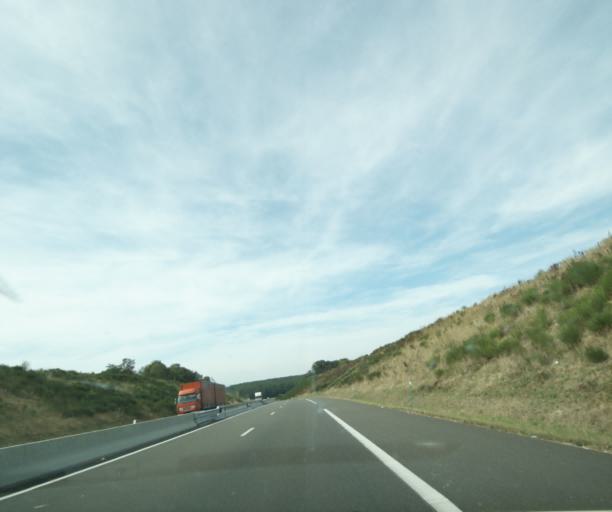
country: FR
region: Auvergne
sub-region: Departement de l'Allier
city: Vendat
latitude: 46.1402
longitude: 3.3458
